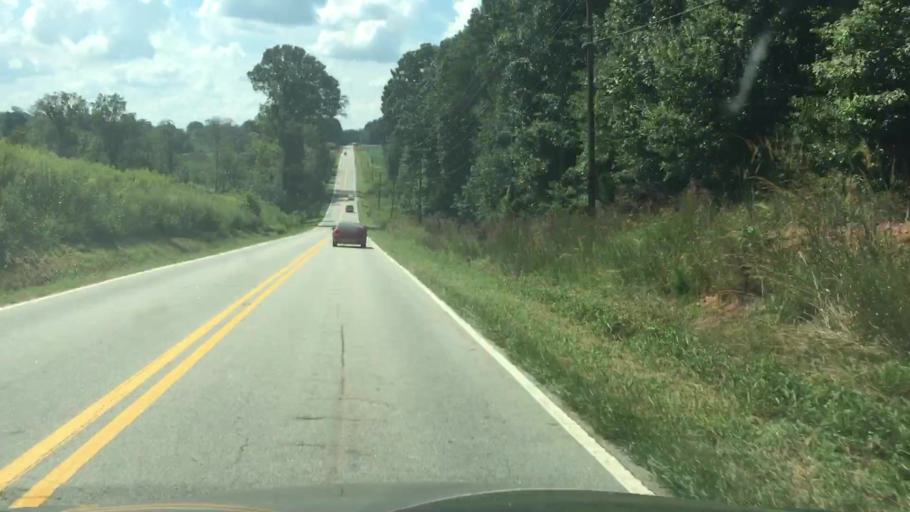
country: US
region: North Carolina
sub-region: Rowan County
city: China Grove
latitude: 35.6496
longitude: -80.6155
